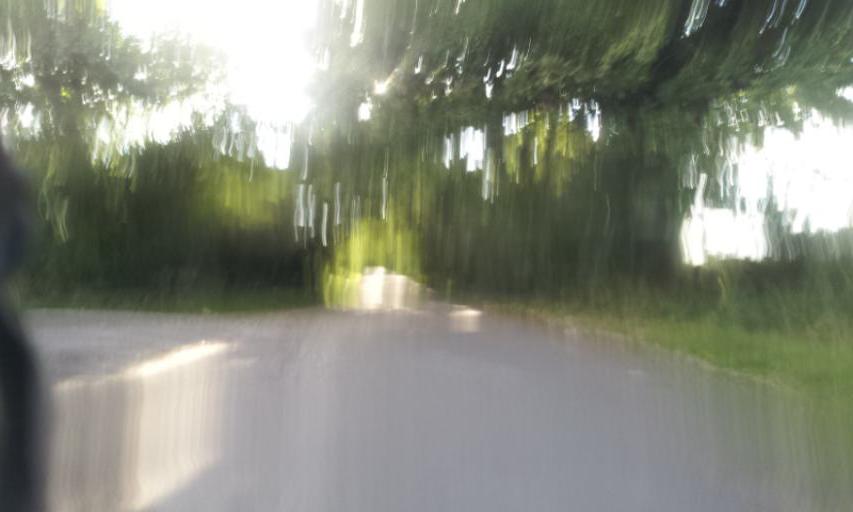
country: GB
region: England
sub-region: Kent
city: Headcorn
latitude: 51.1971
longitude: 0.6343
